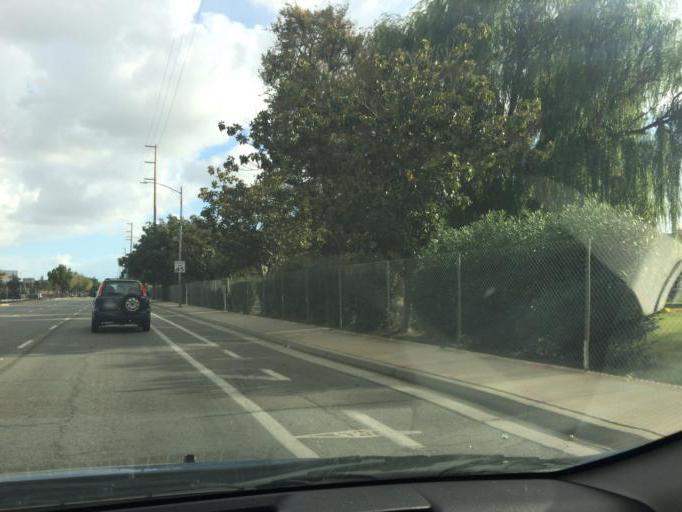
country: US
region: California
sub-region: Santa Clara County
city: Seven Trees
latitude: 37.3004
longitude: -121.8581
